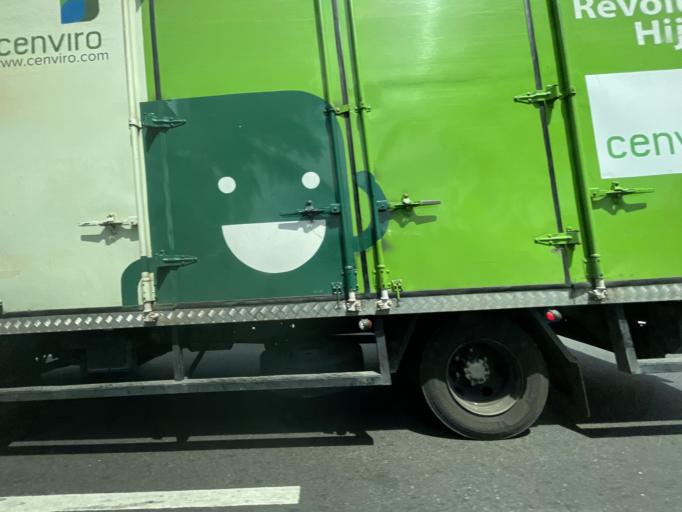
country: MY
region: Melaka
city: Batu Berendam
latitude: 2.2400
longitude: 102.2242
